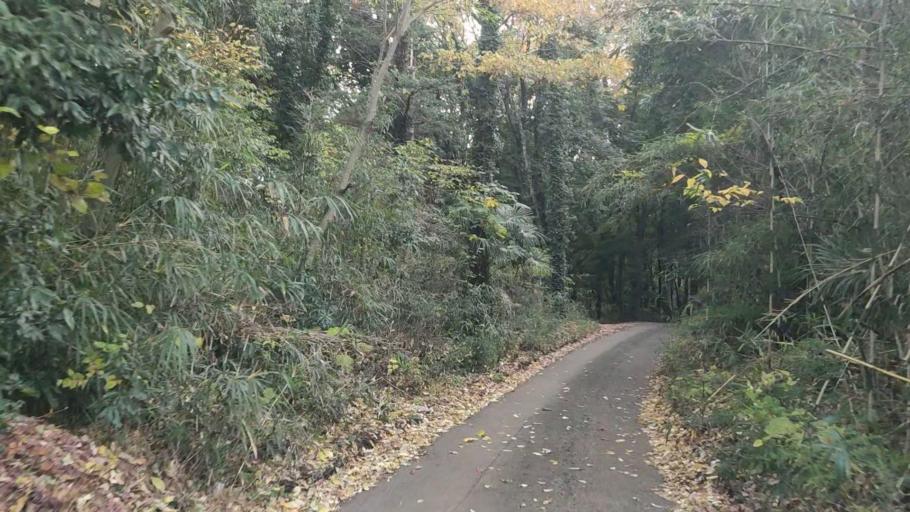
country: JP
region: Kanagawa
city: Minami-rinkan
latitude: 35.4941
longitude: 139.4963
